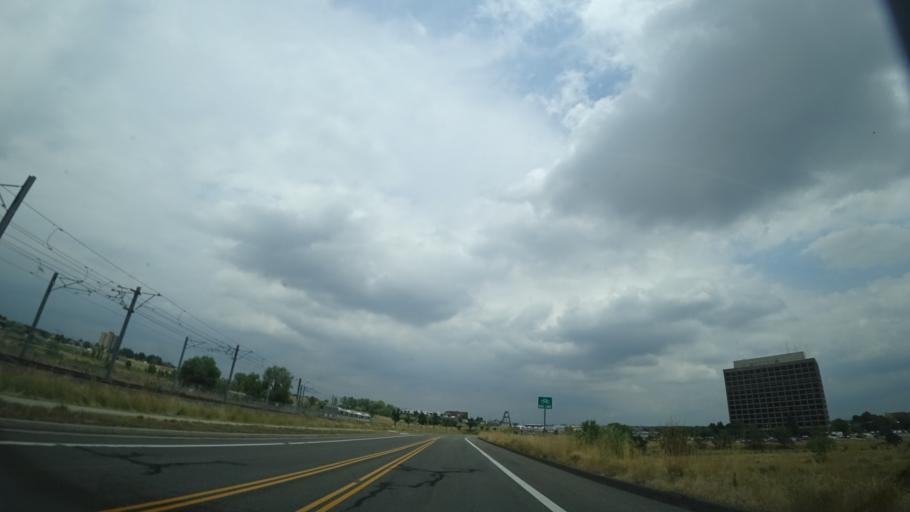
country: US
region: Colorado
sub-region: Jefferson County
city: Lakewood
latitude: 39.7202
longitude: -105.1271
